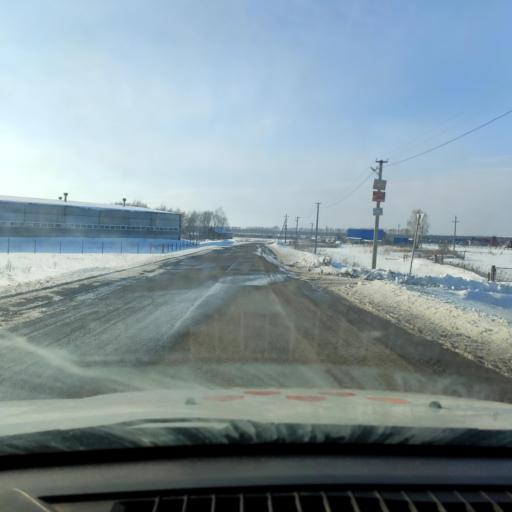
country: RU
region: Bashkortostan
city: Mikhaylovka
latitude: 54.9450
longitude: 55.8655
